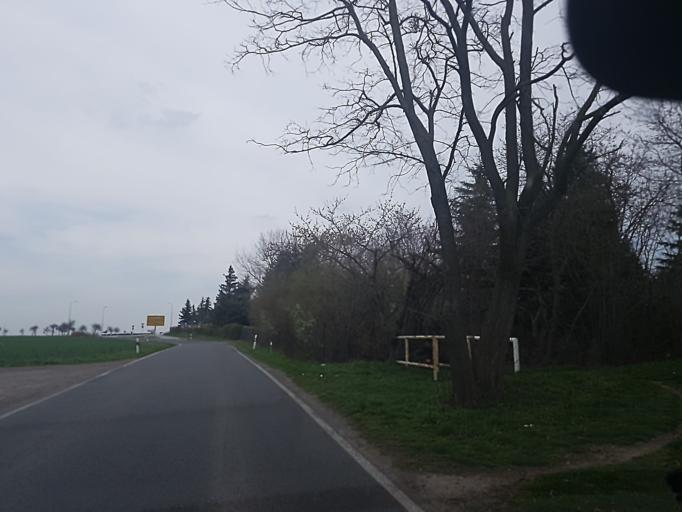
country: DE
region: Saxony
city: Oschatz
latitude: 51.2937
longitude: 13.0925
